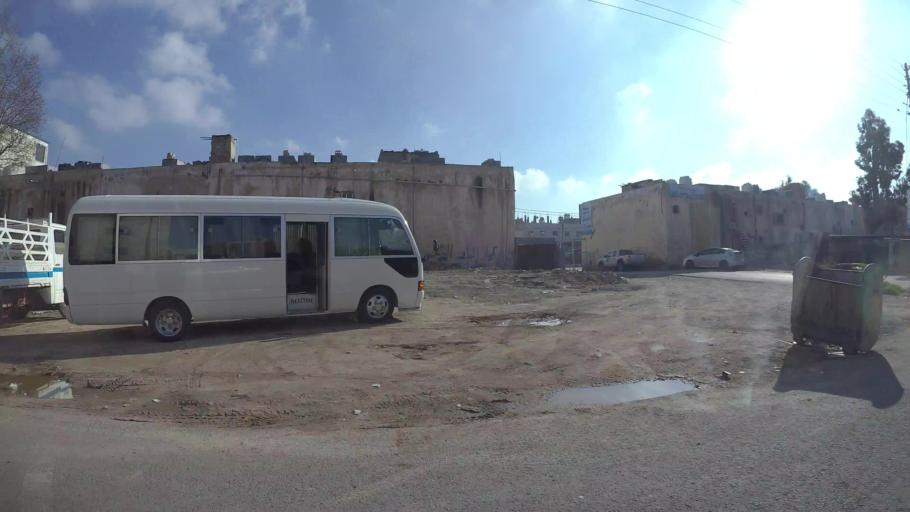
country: JO
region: Amman
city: Al Bunayyat ash Shamaliyah
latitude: 31.8963
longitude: 35.9156
